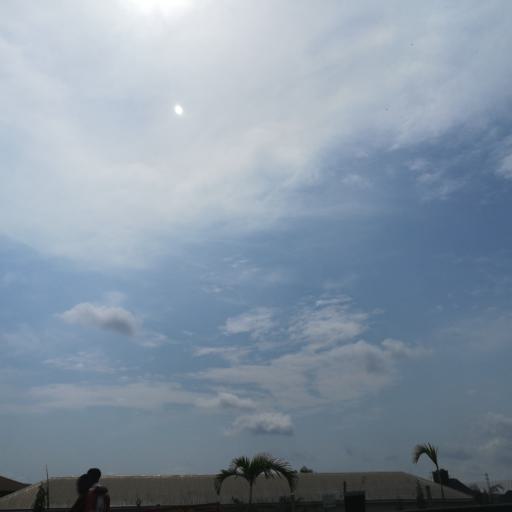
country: NG
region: Rivers
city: Port Harcourt
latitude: 4.8347
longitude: 7.0144
